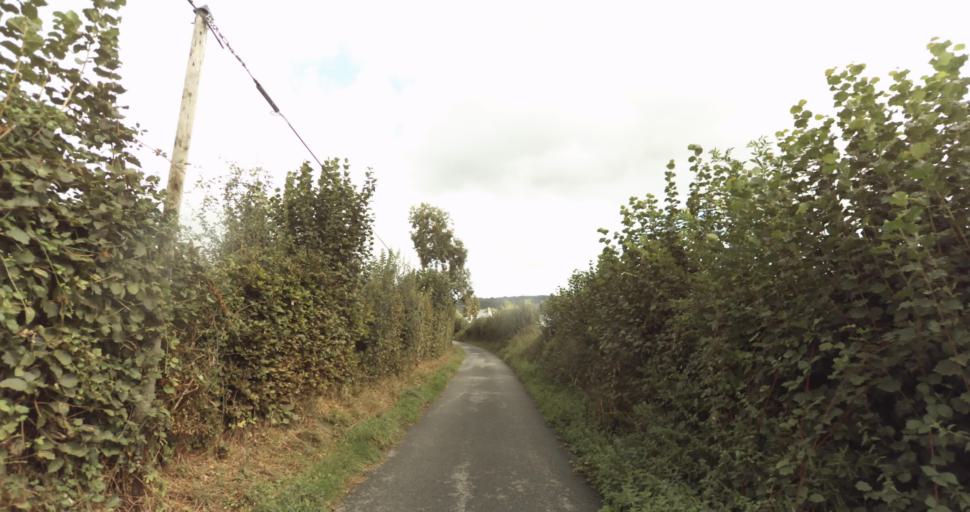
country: FR
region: Lower Normandy
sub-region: Departement de l'Orne
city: Gace
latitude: 48.8037
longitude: 0.2792
